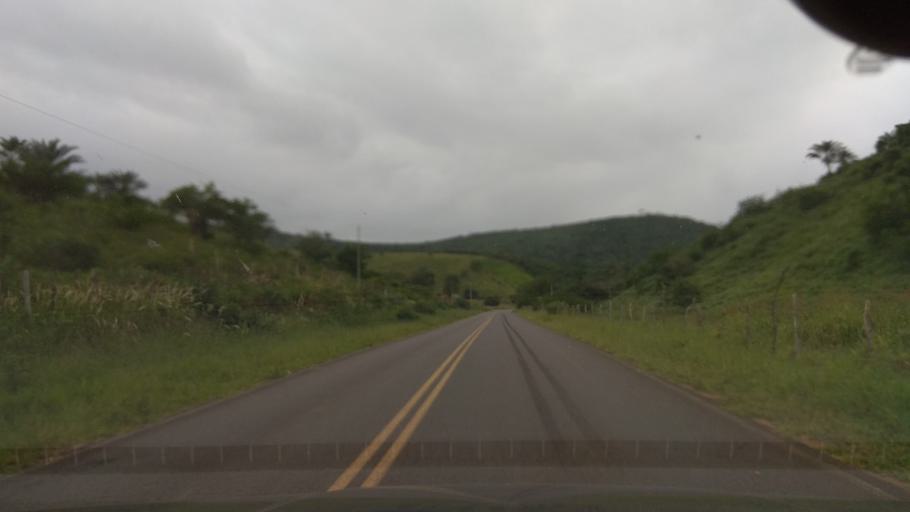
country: BR
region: Bahia
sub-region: Santa Ines
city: Santa Ines
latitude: -13.2669
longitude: -39.7958
